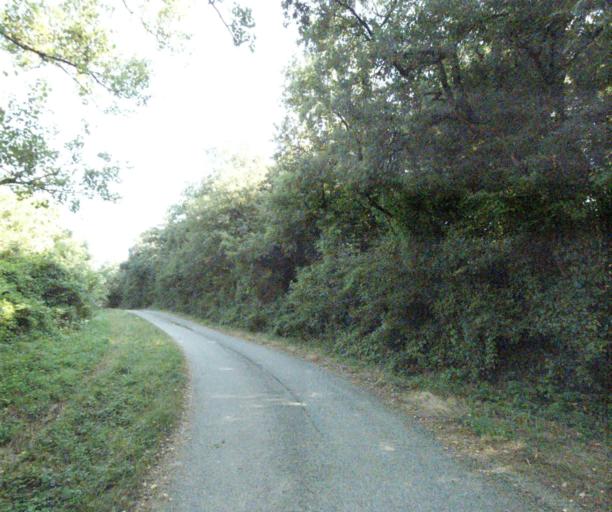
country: FR
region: Midi-Pyrenees
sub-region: Departement de la Haute-Garonne
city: Saint-Felix-Lauragais
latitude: 43.4296
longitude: 1.8280
